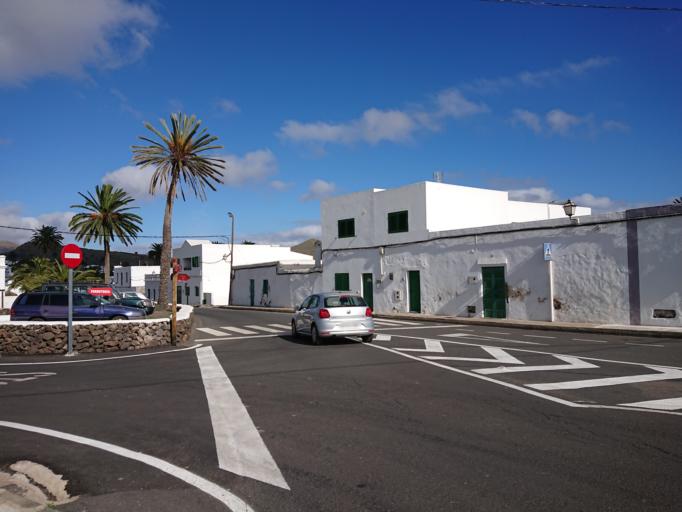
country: ES
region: Canary Islands
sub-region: Provincia de Las Palmas
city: Haria
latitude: 29.1439
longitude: -13.5026
